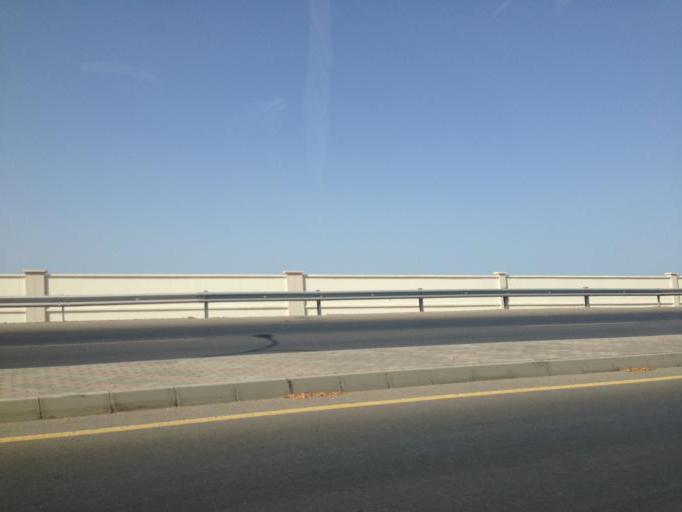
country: OM
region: Muhafazat Masqat
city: As Sib al Jadidah
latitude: 23.6127
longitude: 58.2364
